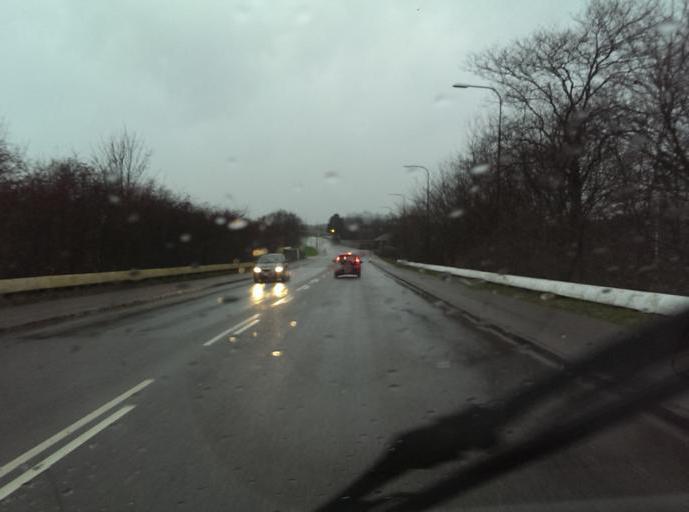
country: DK
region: South Denmark
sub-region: Esbjerg Kommune
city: Esbjerg
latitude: 55.4892
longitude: 8.4602
